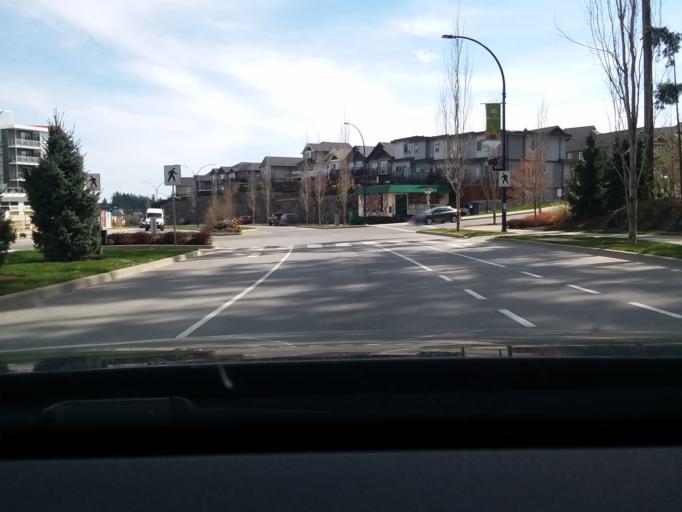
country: CA
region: British Columbia
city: Langford
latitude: 48.4449
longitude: -123.5357
